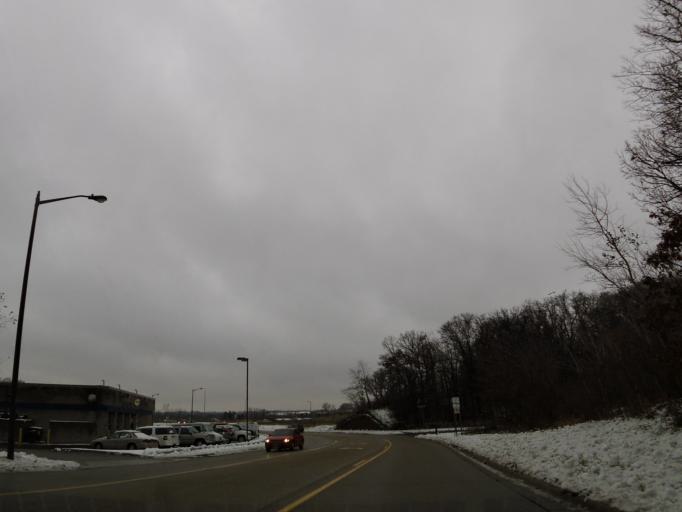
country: US
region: Minnesota
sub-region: Dakota County
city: Lakeville
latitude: 44.6978
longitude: -93.2851
